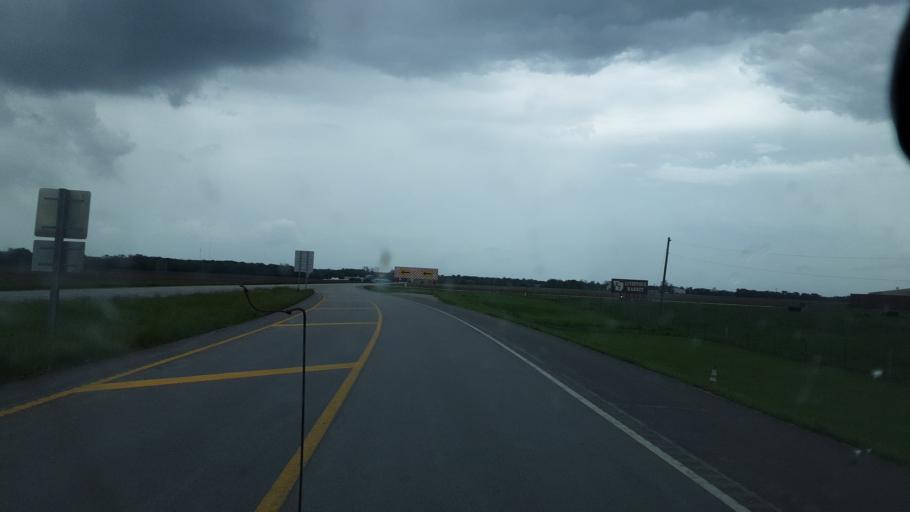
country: US
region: Missouri
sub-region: Marion County
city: Palmyra
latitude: 39.7363
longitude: -91.5099
